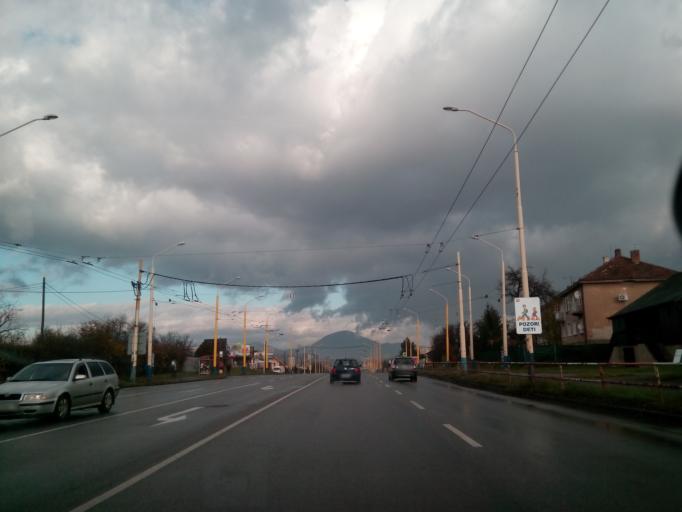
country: SK
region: Presovsky
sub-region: Okres Presov
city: Presov
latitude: 48.9780
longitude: 21.2641
